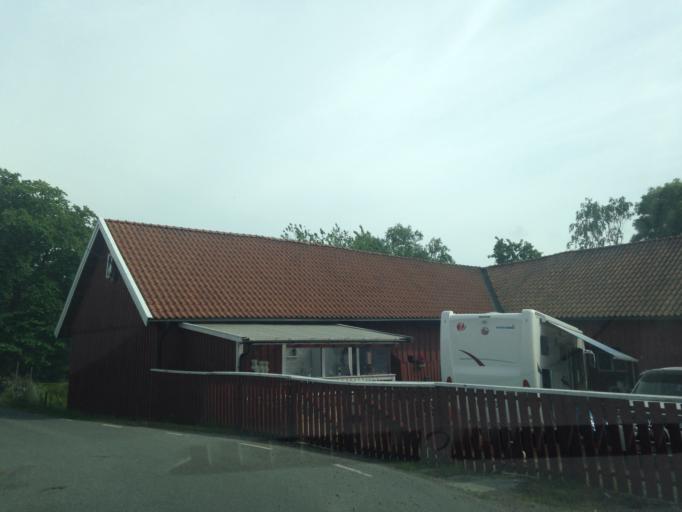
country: SE
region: Vaestra Goetaland
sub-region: Goteborg
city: Majorna
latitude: 57.7556
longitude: 11.8672
